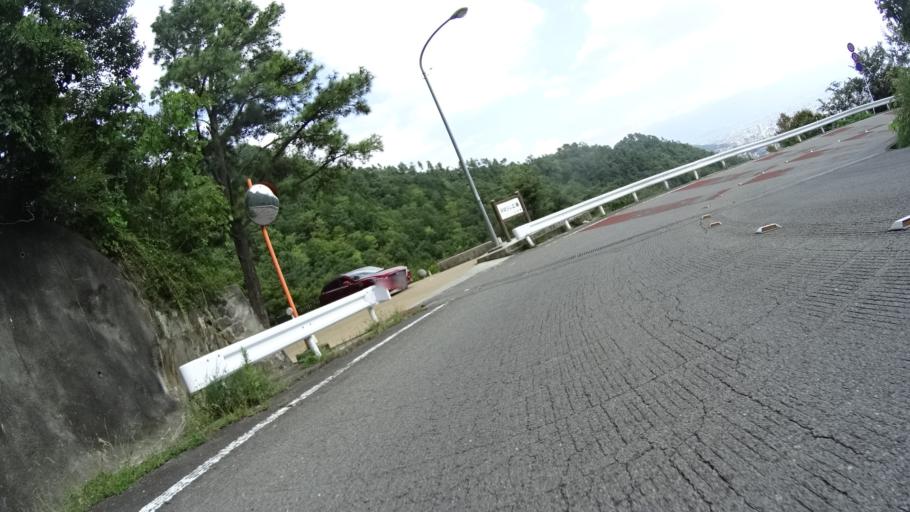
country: JP
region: Yamanashi
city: Kofu-shi
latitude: 35.6986
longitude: 138.5613
